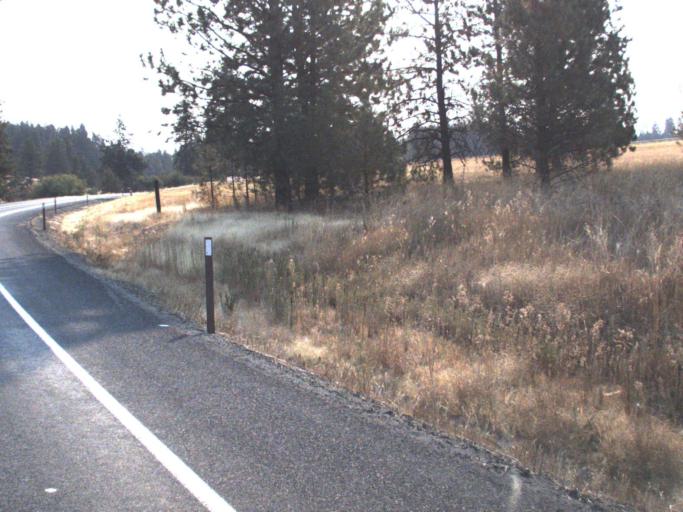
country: US
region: Washington
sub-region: Spokane County
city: Veradale
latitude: 47.4448
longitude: -117.1190
